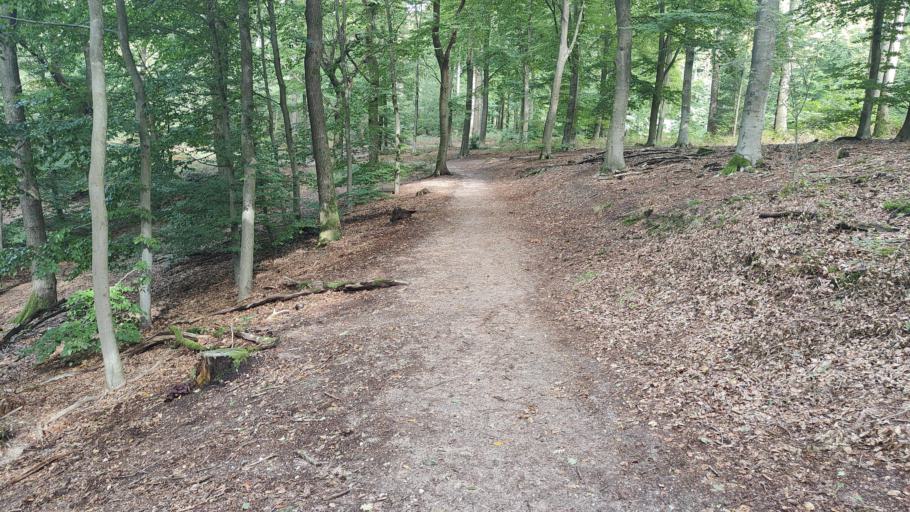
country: NL
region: Gelderland
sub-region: Gemeente Overbetuwe
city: Driel
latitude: 51.9751
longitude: 5.8173
